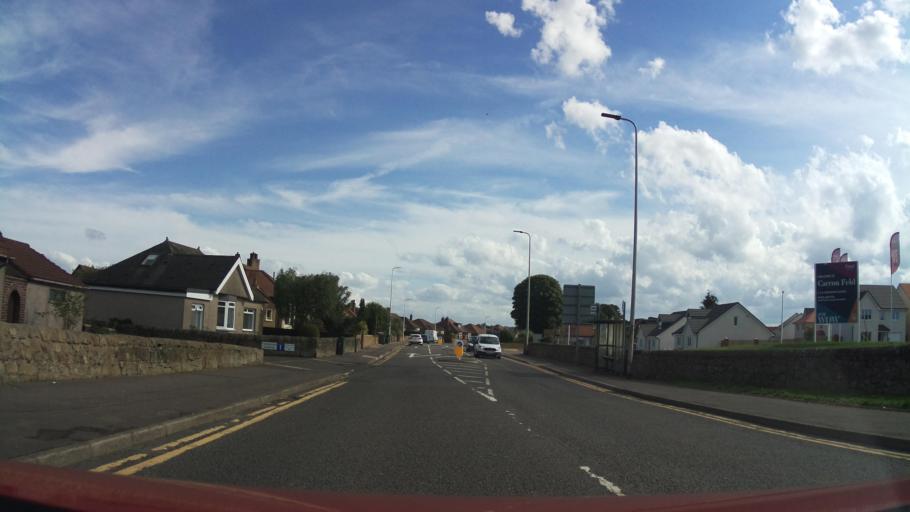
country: GB
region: Scotland
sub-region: Falkirk
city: Larbert
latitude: 56.0251
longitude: -3.8389
